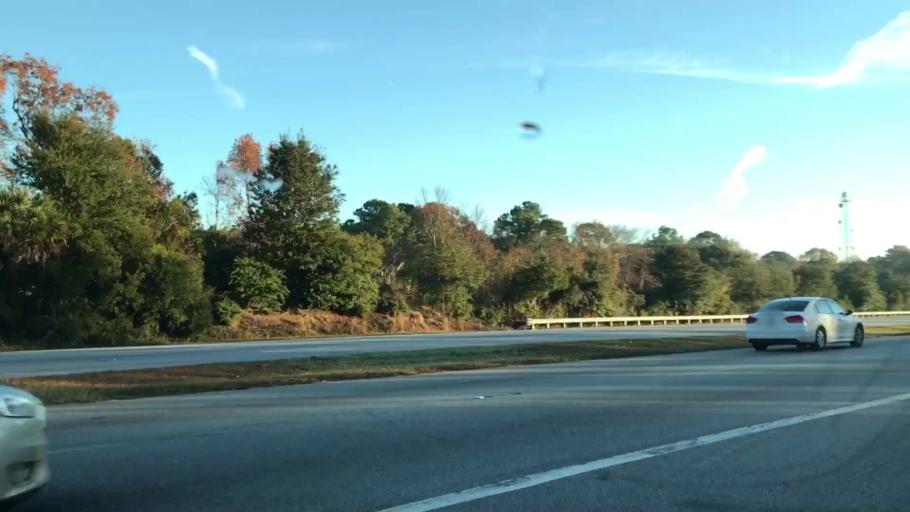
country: US
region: South Carolina
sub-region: Charleston County
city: Shell Point
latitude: 32.8113
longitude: -80.0516
